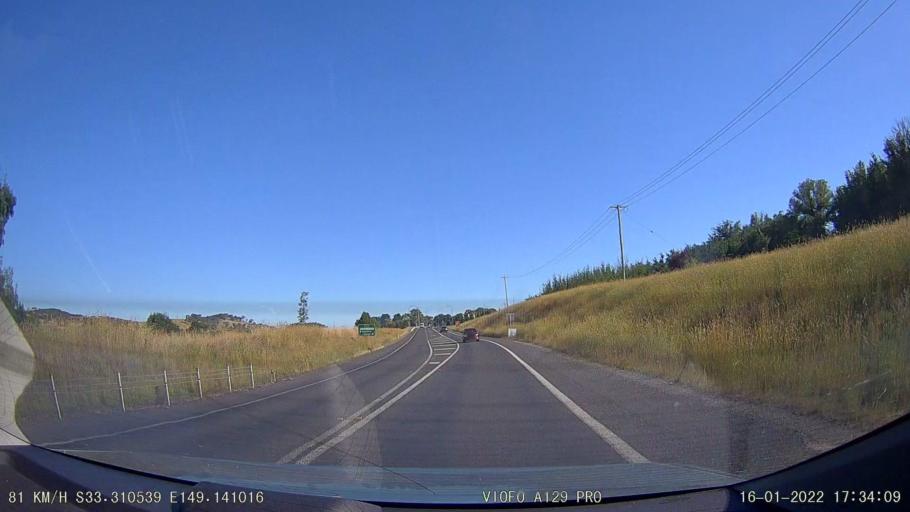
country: AU
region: New South Wales
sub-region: Orange Municipality
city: Orange
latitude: -33.3104
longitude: 149.1410
